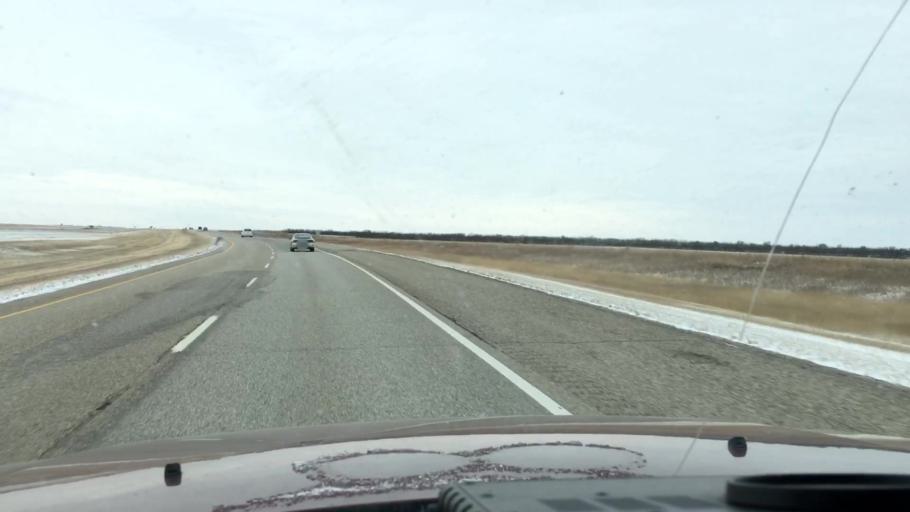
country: CA
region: Saskatchewan
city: Saskatoon
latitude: 51.4708
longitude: -106.2472
